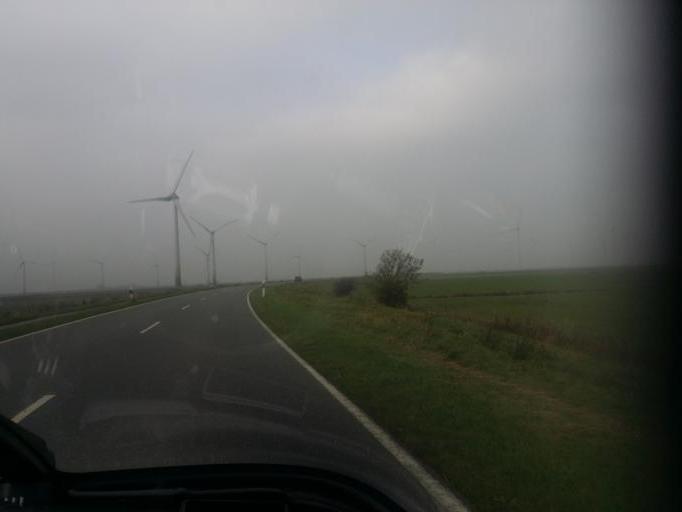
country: DE
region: Schleswig-Holstein
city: Langenhorn
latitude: 54.6449
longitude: 8.8999
